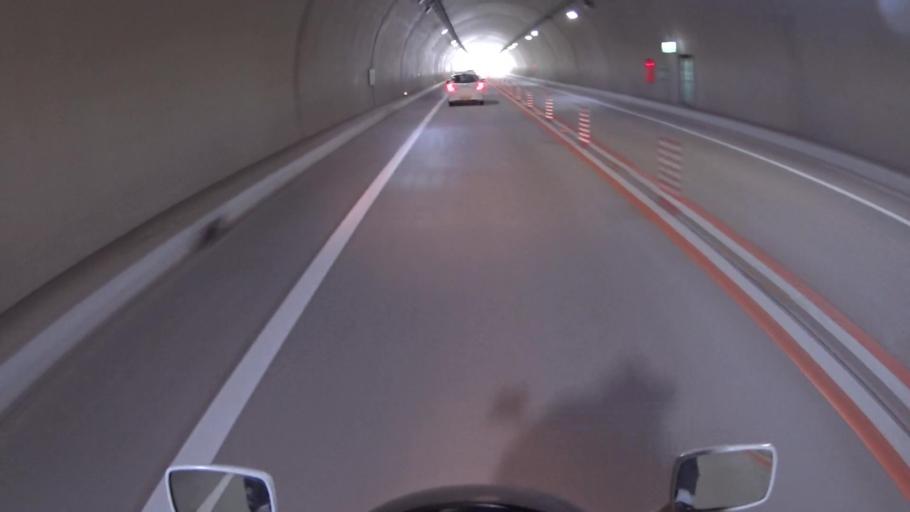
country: JP
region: Kyoto
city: Ayabe
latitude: 35.2077
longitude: 135.3472
